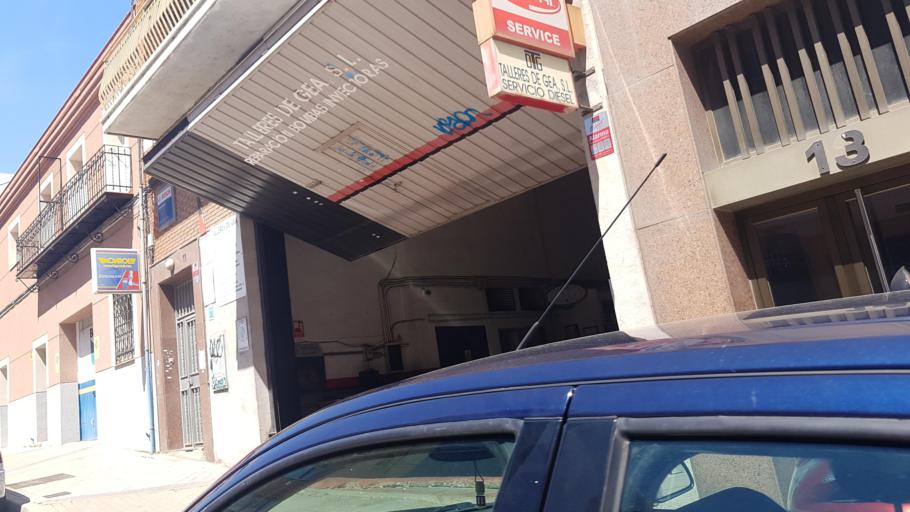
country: ES
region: Madrid
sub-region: Provincia de Madrid
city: San Blas
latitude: 40.4397
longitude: -3.6274
